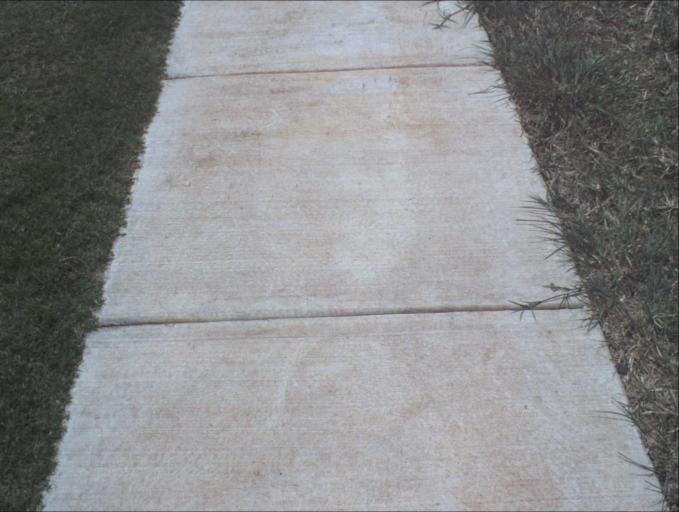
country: AU
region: Queensland
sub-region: Logan
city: Rochedale South
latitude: -27.6020
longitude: 153.1043
